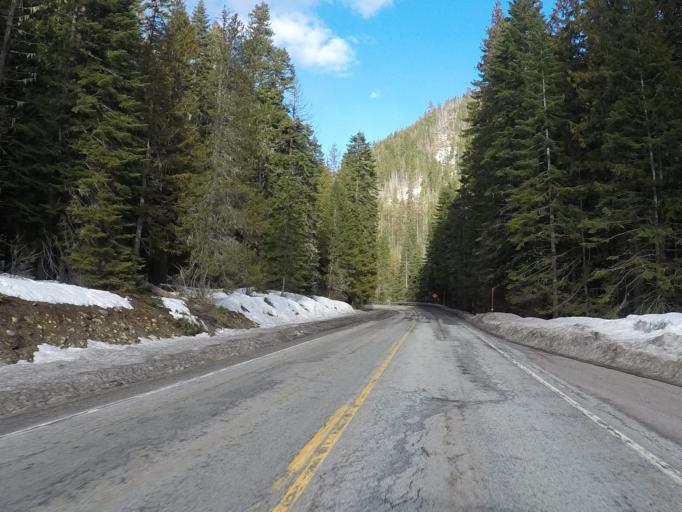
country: US
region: Montana
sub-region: Mineral County
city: Superior
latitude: 46.4882
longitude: -114.8728
